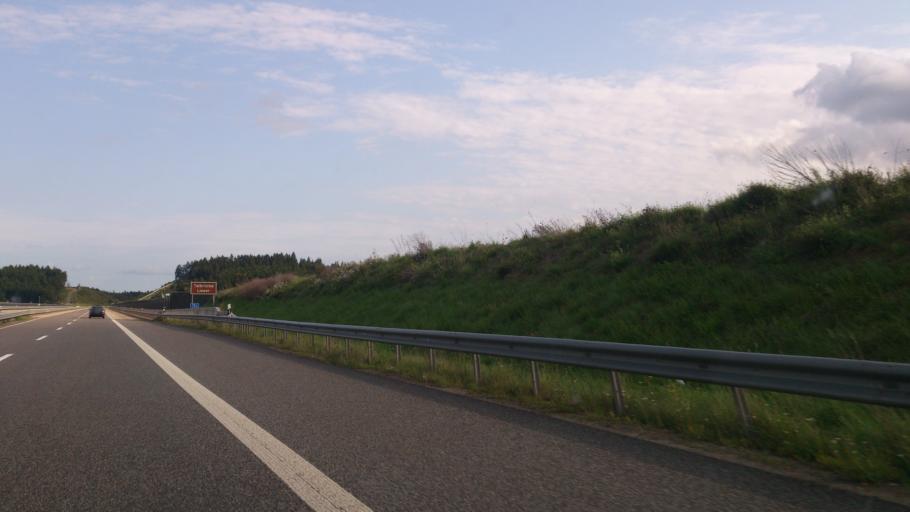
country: DE
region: Rheinland-Pfalz
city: Nerdlen
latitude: 50.2305
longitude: 6.8474
